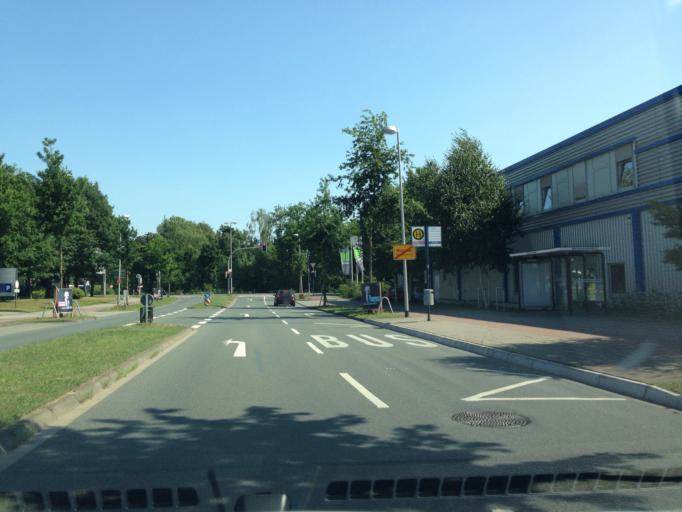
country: DE
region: North Rhine-Westphalia
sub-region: Regierungsbezirk Munster
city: Muenster
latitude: 51.9582
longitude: 7.5716
